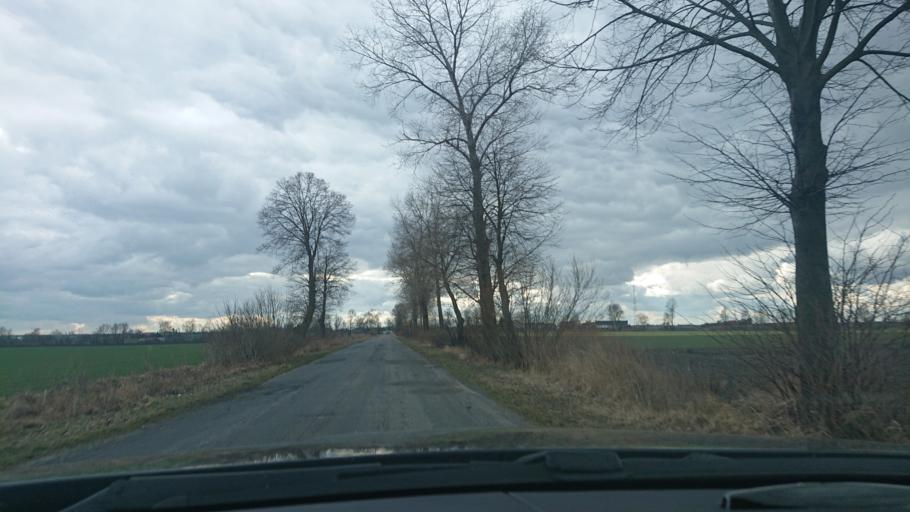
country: PL
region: Greater Poland Voivodeship
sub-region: Powiat gnieznienski
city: Niechanowo
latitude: 52.5875
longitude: 17.6961
